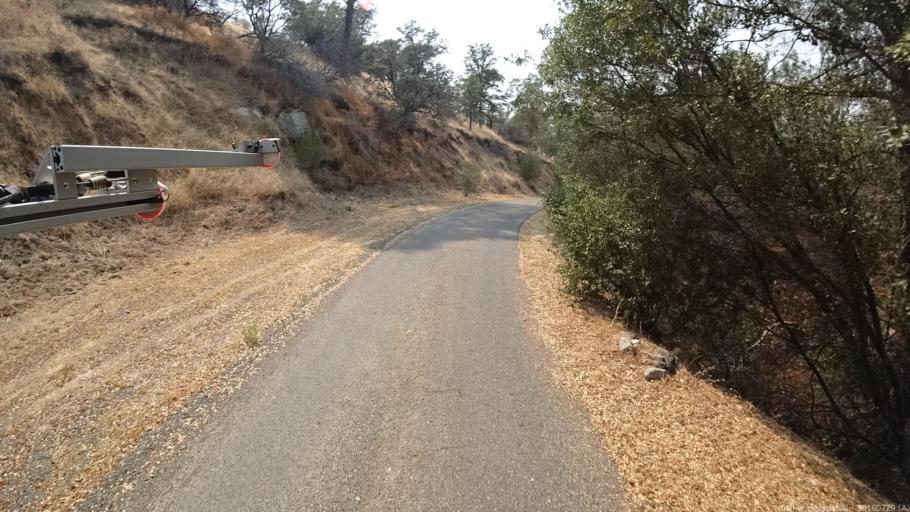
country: US
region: California
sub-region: Madera County
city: Yosemite Lakes
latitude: 37.2196
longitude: -119.7639
